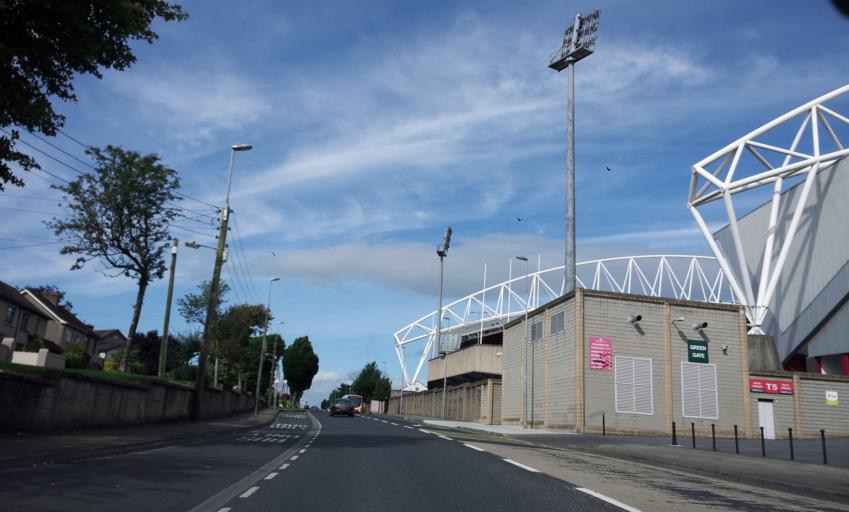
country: IE
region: Munster
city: Moyross
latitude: 52.6732
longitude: -8.6410
